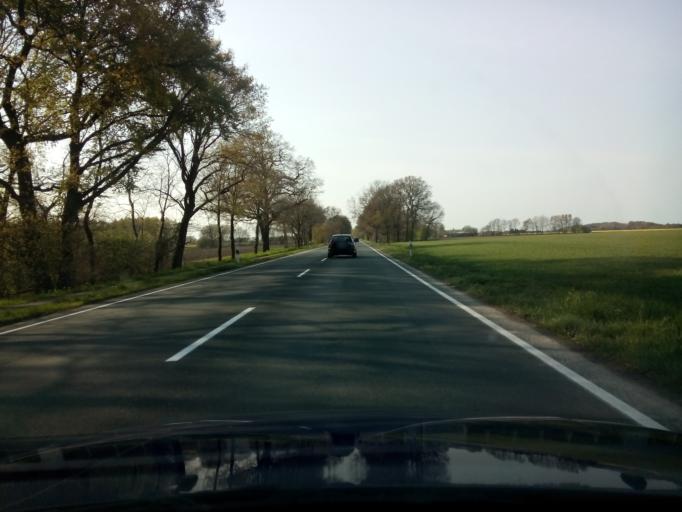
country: DE
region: Lower Saxony
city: Sustedt
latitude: 52.8522
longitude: 8.8918
